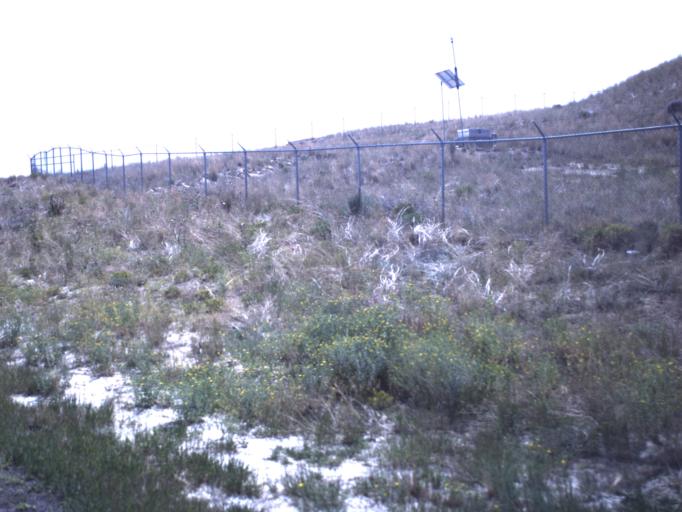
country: US
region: Utah
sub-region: Daggett County
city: Manila
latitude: 40.9796
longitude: -109.8087
